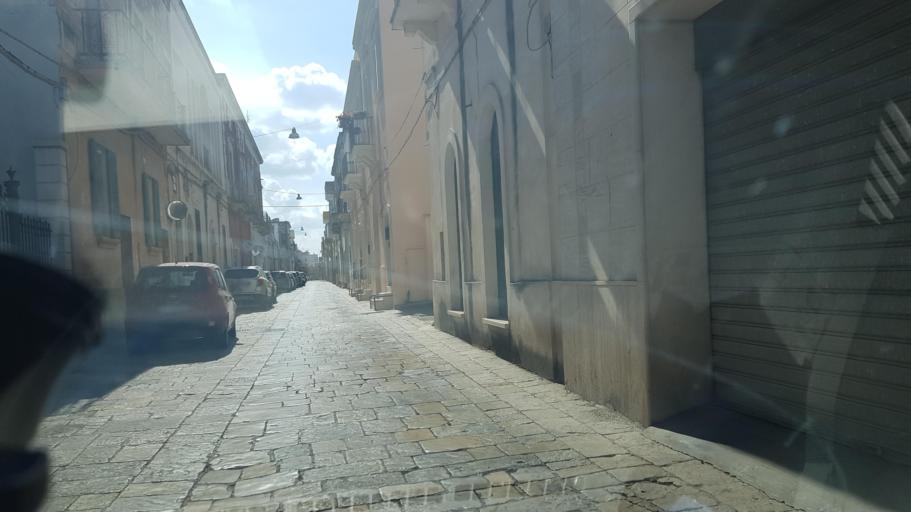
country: IT
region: Apulia
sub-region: Provincia di Brindisi
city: Mesagne
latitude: 40.5567
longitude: 17.8123
